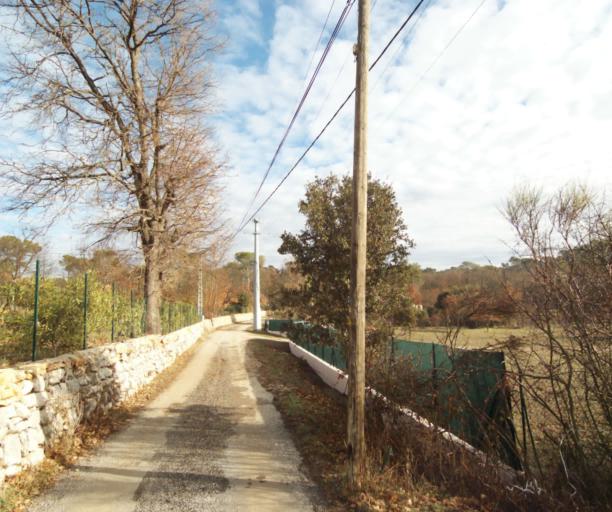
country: FR
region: Provence-Alpes-Cote d'Azur
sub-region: Departement du Var
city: Trans-en-Provence
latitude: 43.4934
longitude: 6.4736
